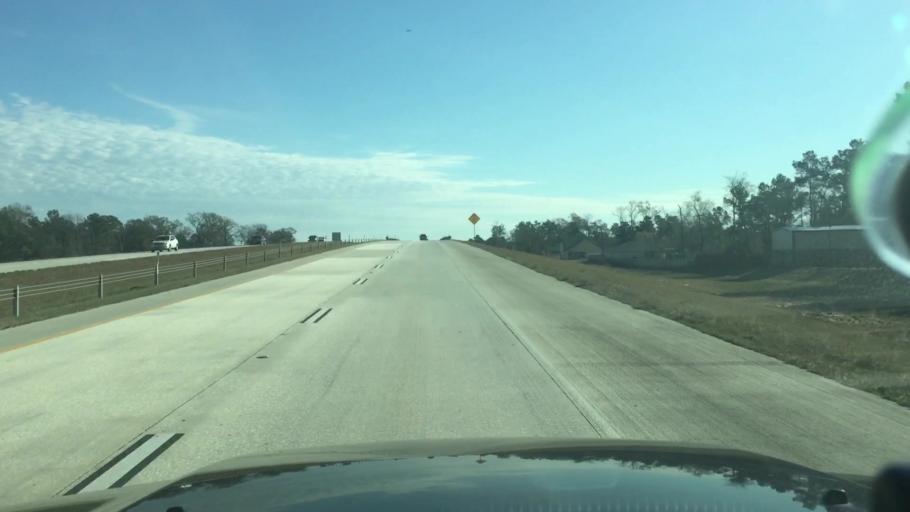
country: US
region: Texas
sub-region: Montgomery County
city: Porter Heights
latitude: 30.1376
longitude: -95.2749
